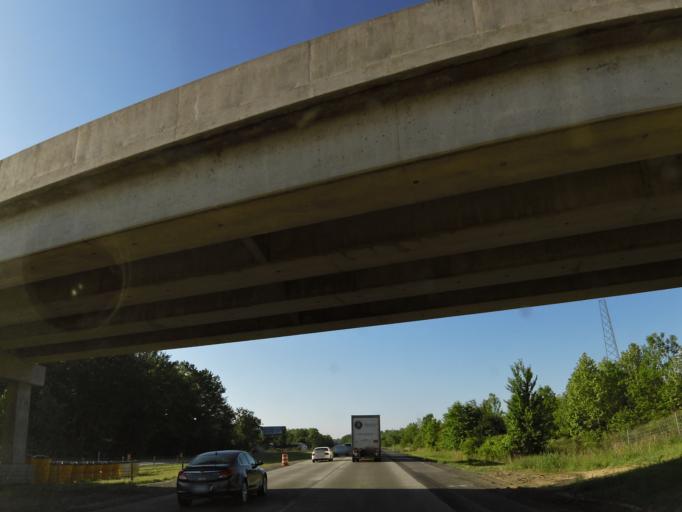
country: US
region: Indiana
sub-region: Jackson County
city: Seymour
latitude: 38.9221
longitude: -85.8370
